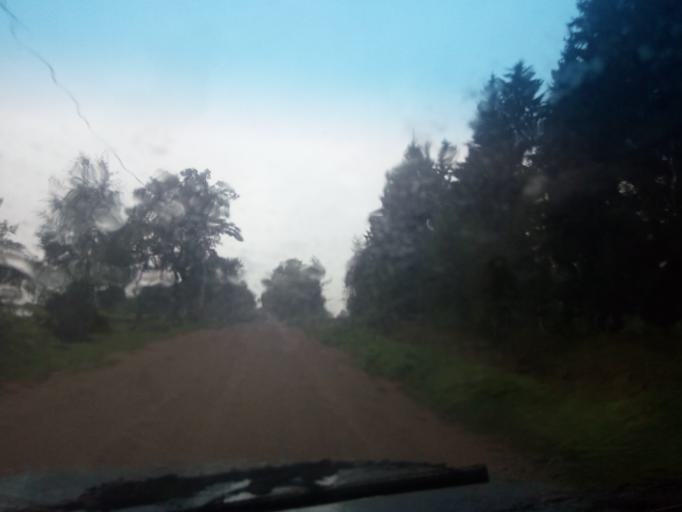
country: BY
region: Vitebsk
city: Dzisna
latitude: 55.6722
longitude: 28.3189
